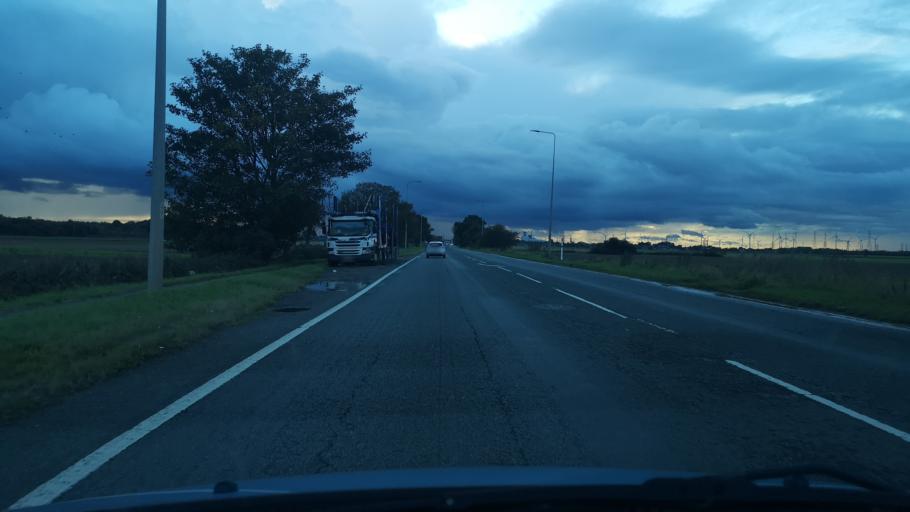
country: GB
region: England
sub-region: North Lincolnshire
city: Gunness
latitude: 53.5895
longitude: -0.7043
